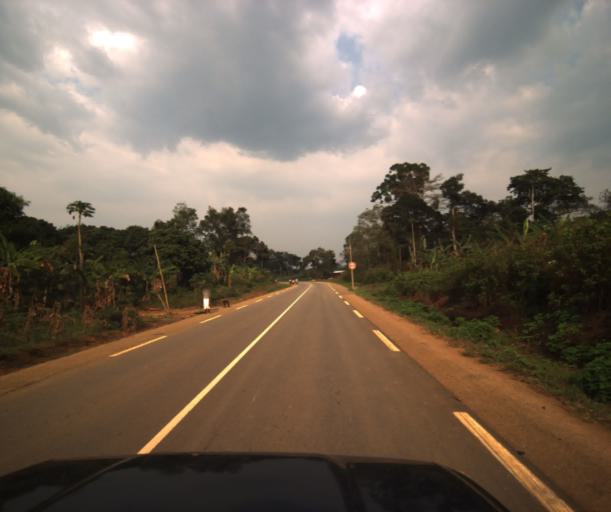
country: CM
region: Centre
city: Mbankomo
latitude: 3.7433
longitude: 11.3975
